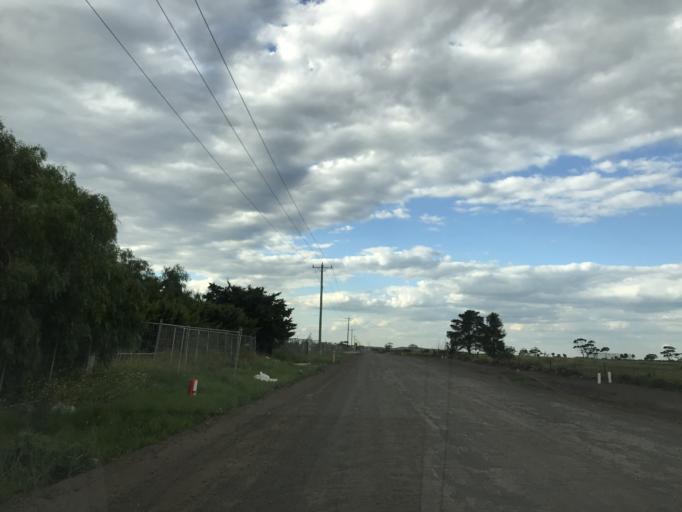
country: AU
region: Victoria
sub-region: Wyndham
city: Truganina
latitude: -37.8212
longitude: 144.7216
